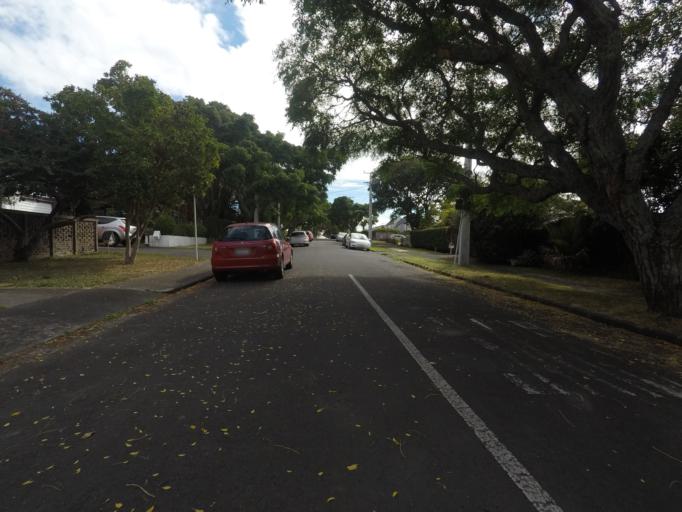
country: NZ
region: Auckland
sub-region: Auckland
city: Auckland
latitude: -36.8794
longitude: 174.7204
